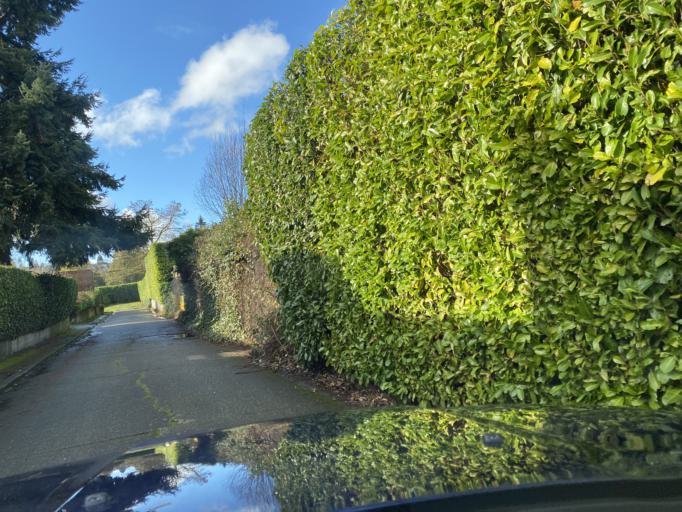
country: US
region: Washington
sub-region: King County
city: Seattle
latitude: 47.6295
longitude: -122.2896
